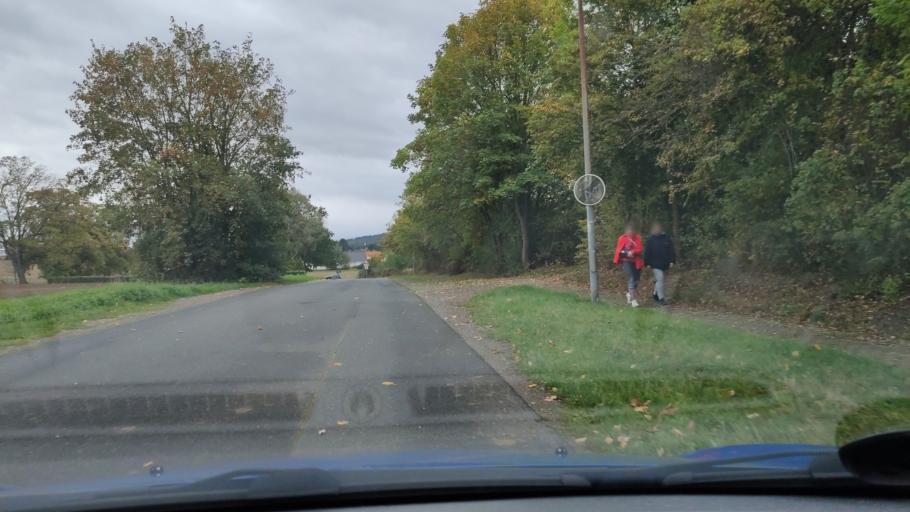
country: DE
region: Lower Saxony
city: Seelze
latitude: 52.3790
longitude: 9.6512
